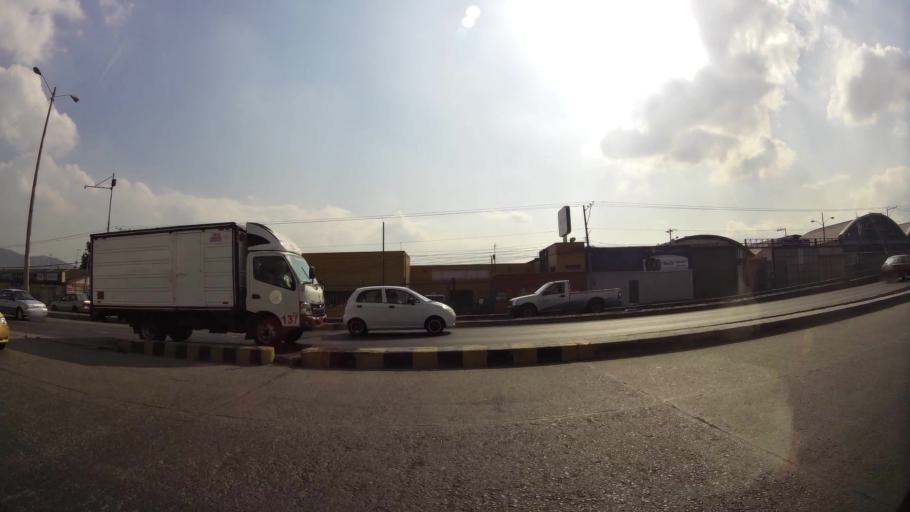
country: EC
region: Guayas
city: Guayaquil
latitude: -2.1321
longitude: -79.9332
